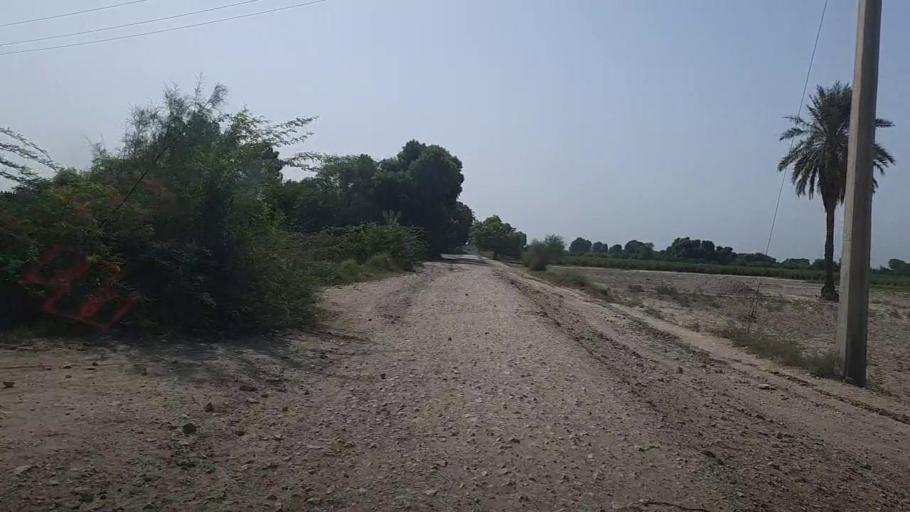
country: PK
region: Sindh
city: Pad Idan
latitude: 26.7633
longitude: 68.3320
